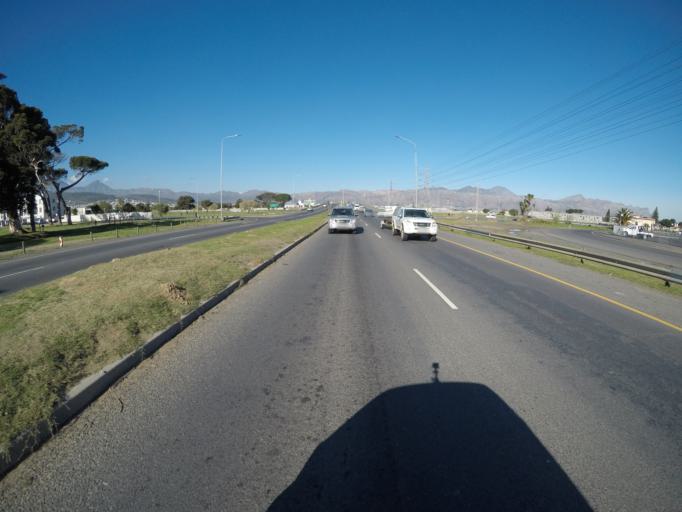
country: ZA
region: Western Cape
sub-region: Cape Winelands District Municipality
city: Stellenbosch
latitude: -34.0983
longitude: 18.8489
